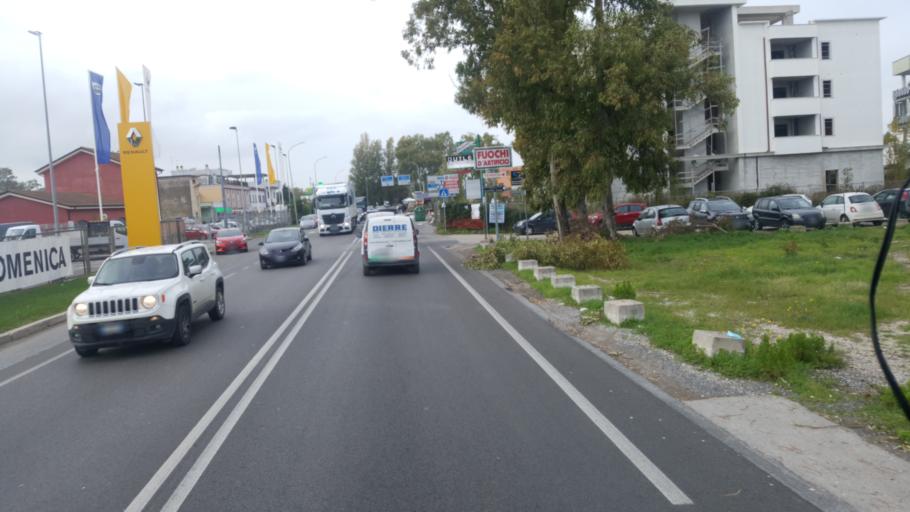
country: IT
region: Latium
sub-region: Provincia di Latina
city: Borgo Podgora
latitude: 41.4810
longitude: 12.8665
